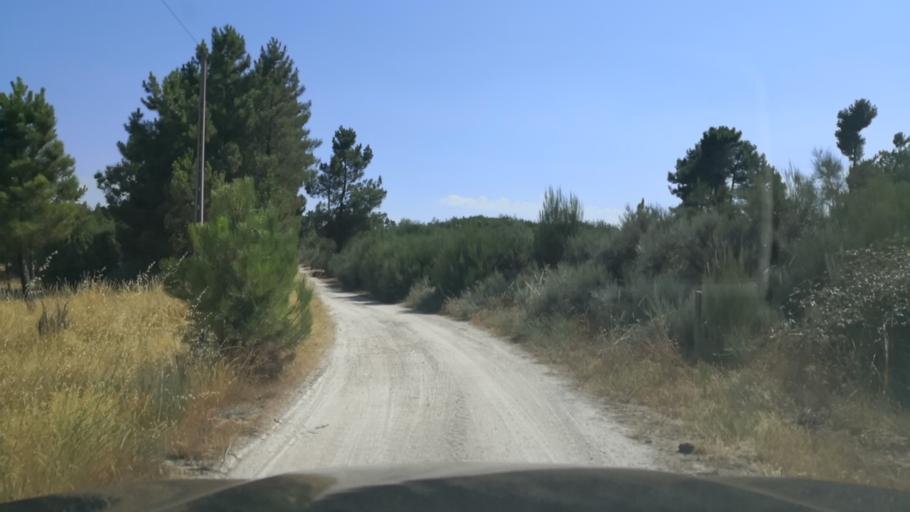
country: PT
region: Vila Real
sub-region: Murca
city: Murca
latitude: 41.3423
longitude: -7.4754
